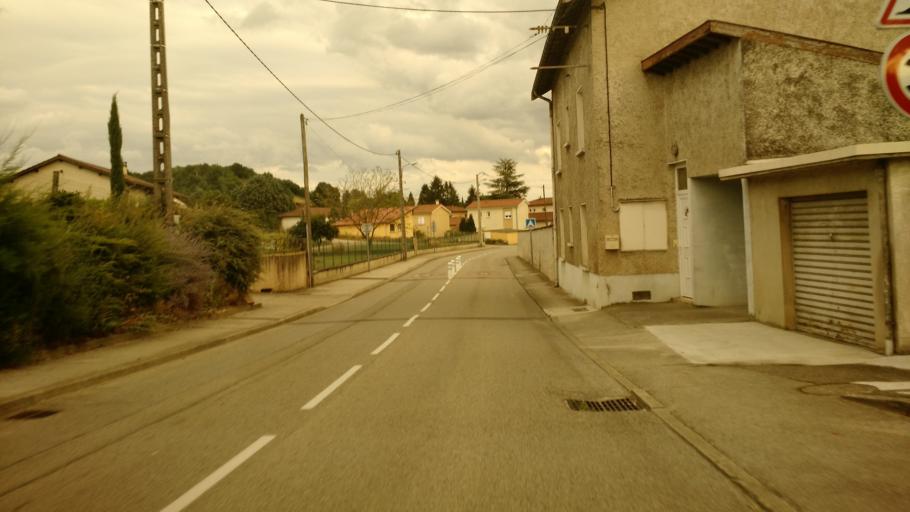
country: FR
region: Rhone-Alpes
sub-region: Departement de l'Ain
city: Montluel
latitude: 45.8566
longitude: 5.0578
